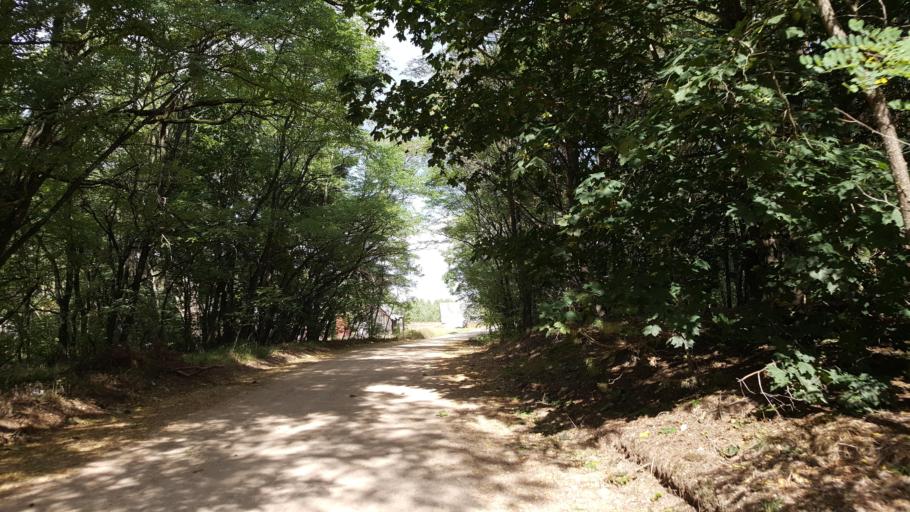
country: BY
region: Brest
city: Kamyanyets
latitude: 52.4375
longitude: 23.9402
